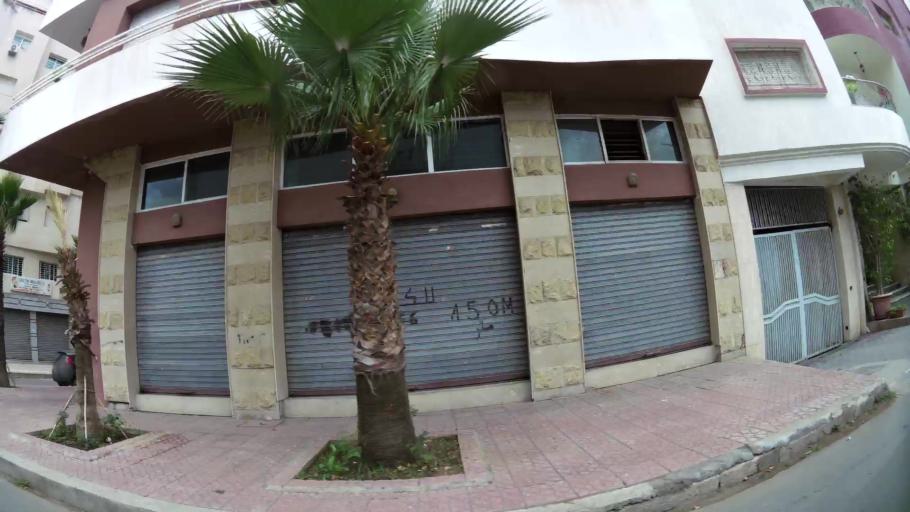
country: MA
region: Gharb-Chrarda-Beni Hssen
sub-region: Kenitra Province
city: Kenitra
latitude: 34.2548
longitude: -6.5829
